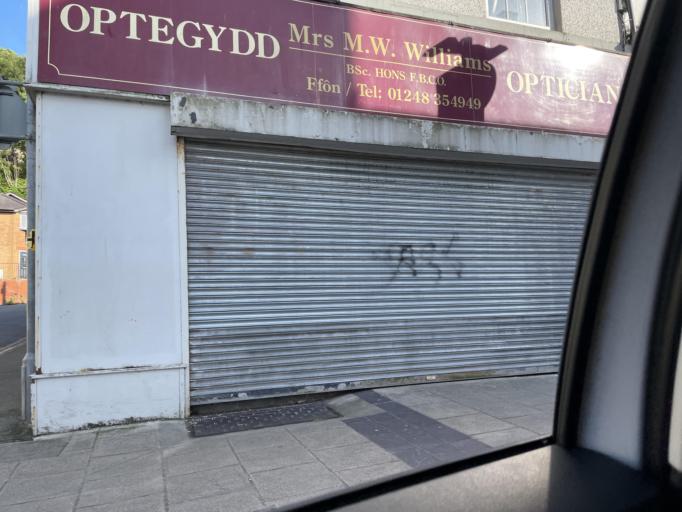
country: GB
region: Wales
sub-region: Gwynedd
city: Bangor
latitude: 53.2284
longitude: -4.1229
